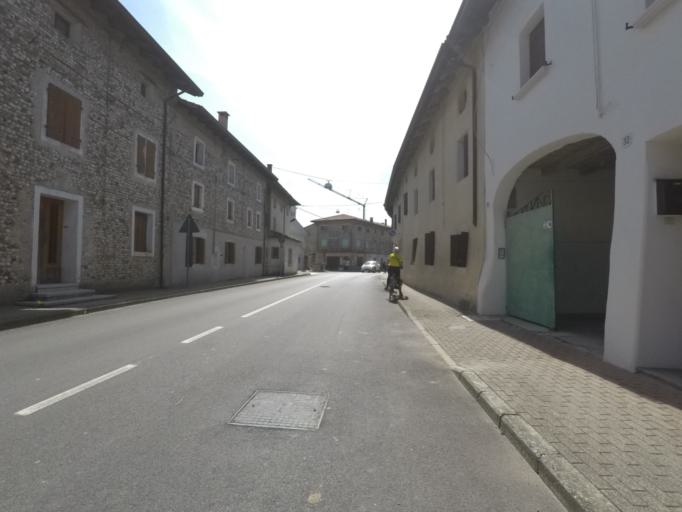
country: IT
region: Friuli Venezia Giulia
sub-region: Provincia di Pordenone
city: Casarsa della Delizia
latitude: 45.9413
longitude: 12.8351
